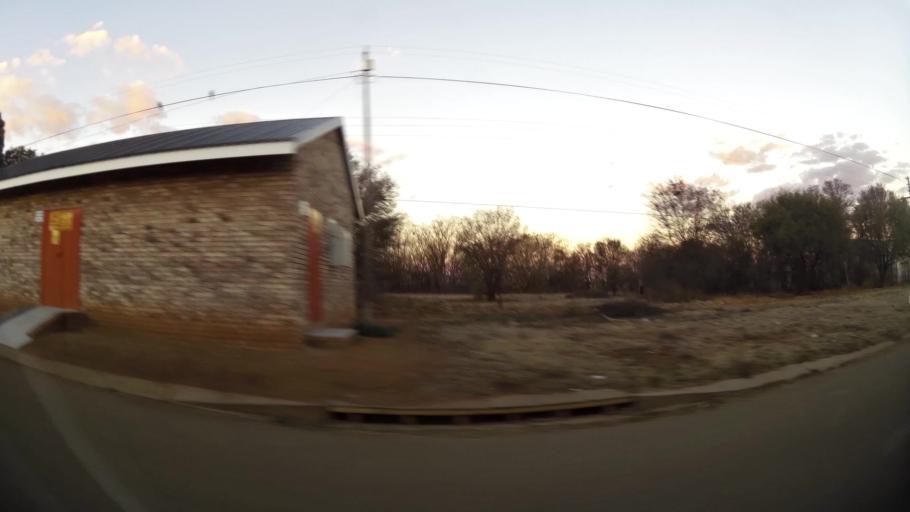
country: ZA
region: North-West
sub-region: Dr Kenneth Kaunda District Municipality
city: Potchefstroom
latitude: -26.7159
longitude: 27.1235
